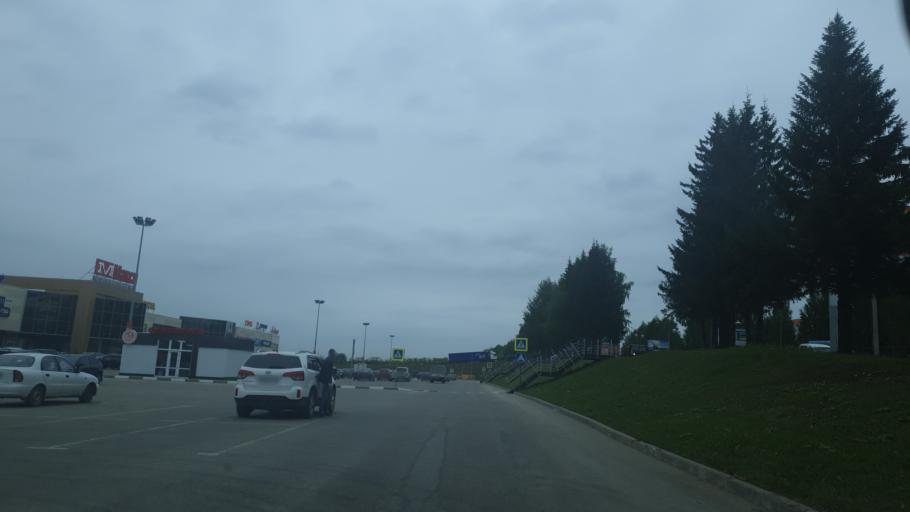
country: RU
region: Komi Republic
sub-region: Syktyvdinskiy Rayon
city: Syktyvkar
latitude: 61.6975
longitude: 50.8048
